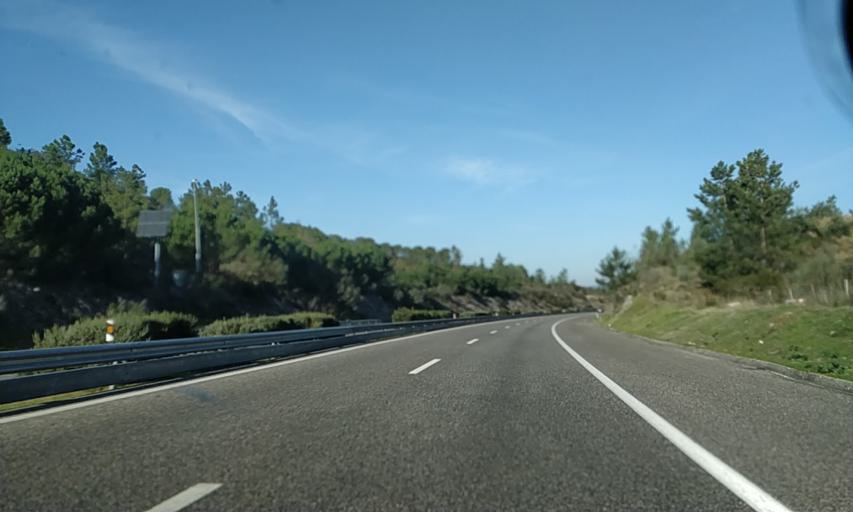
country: PT
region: Coimbra
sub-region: Condeixa-A-Nova
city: Condeixa-a-Nova
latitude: 40.0824
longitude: -8.5373
